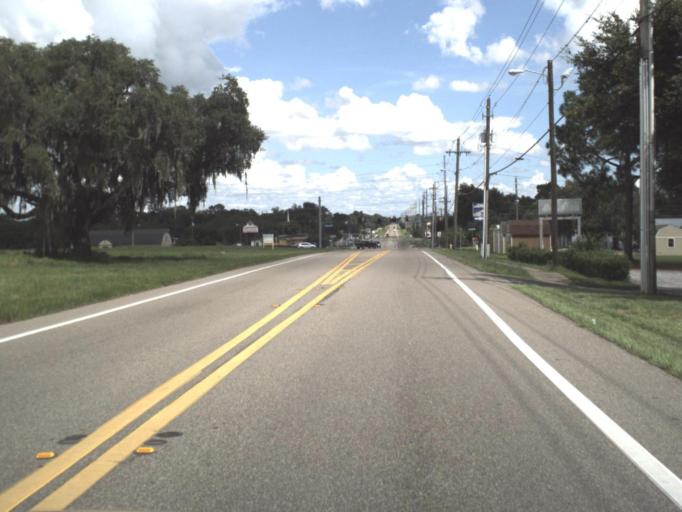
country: US
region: Florida
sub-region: Polk County
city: Cypress Gardens
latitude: 28.0225
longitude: -81.6962
